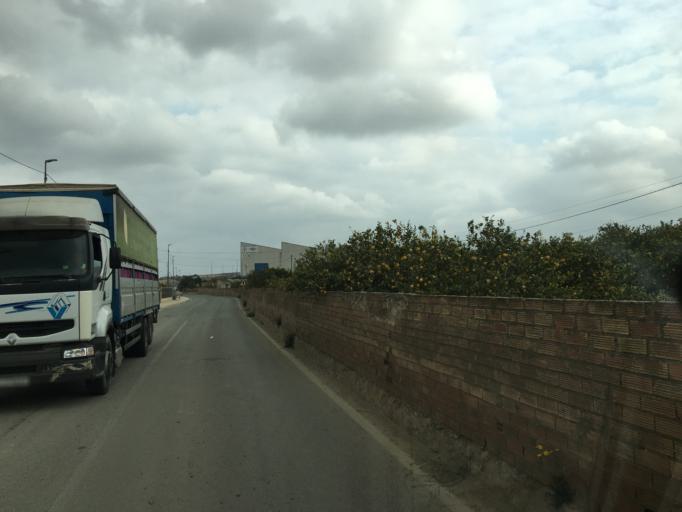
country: ES
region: Murcia
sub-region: Murcia
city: Beniel
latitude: 38.0174
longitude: -0.9861
